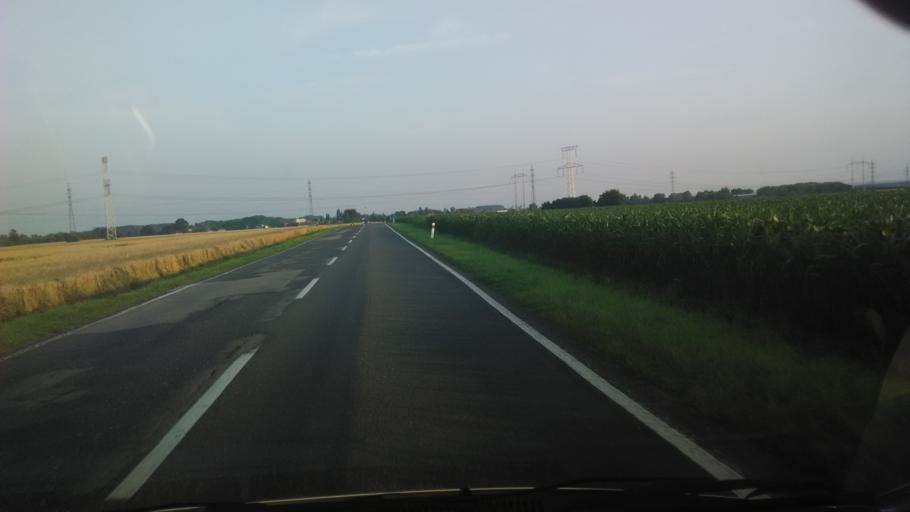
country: SK
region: Nitriansky
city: Tlmace
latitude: 48.2212
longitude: 18.5195
